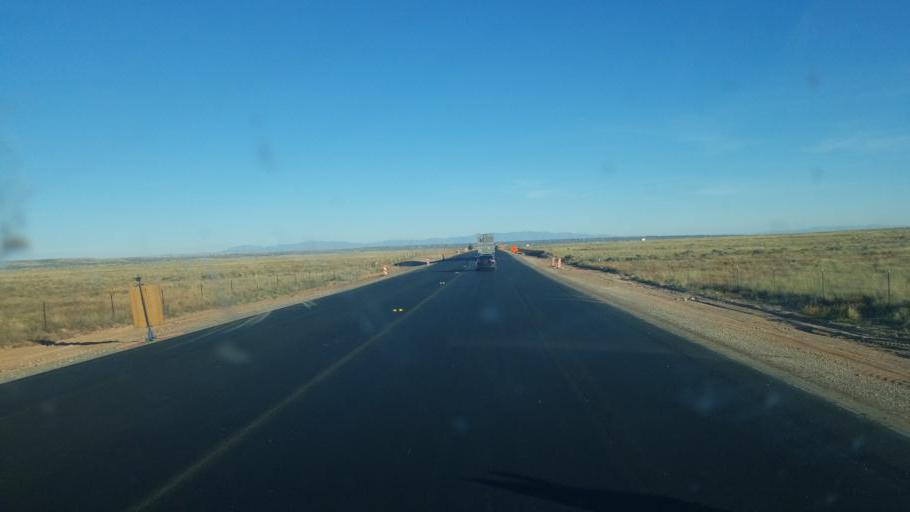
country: US
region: New Mexico
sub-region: Cibola County
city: Laguna
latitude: 34.8877
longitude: -107.0719
